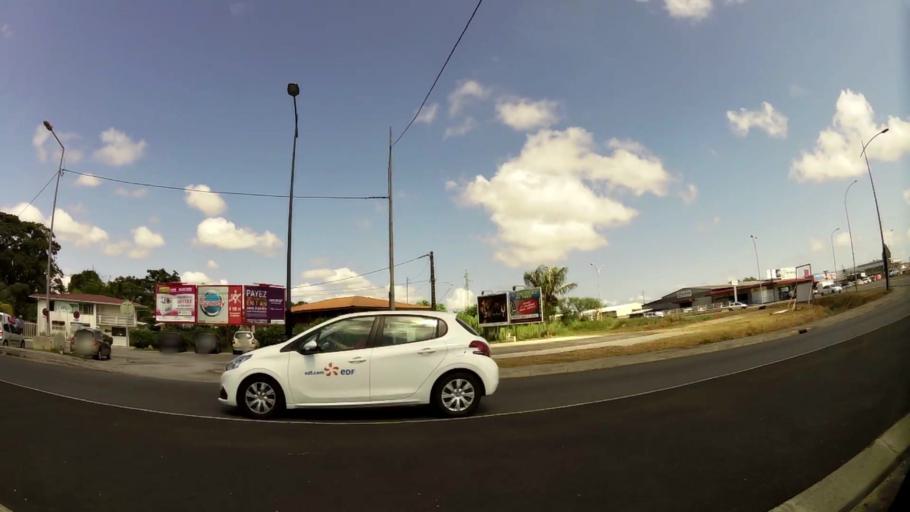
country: GF
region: Guyane
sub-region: Guyane
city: Cayenne
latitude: 4.9237
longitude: -52.3239
